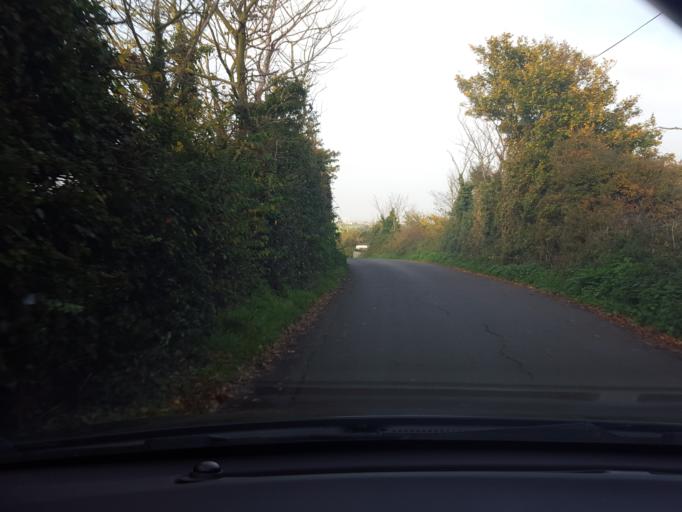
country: GB
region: England
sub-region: Essex
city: Walton-on-the-Naze
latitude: 51.8515
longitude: 1.2563
